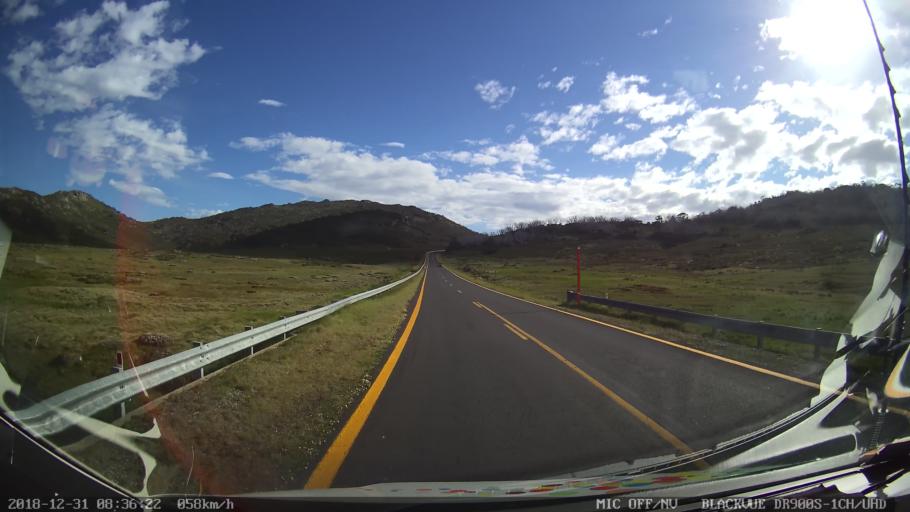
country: AU
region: New South Wales
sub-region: Snowy River
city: Jindabyne
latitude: -36.4253
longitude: 148.3765
